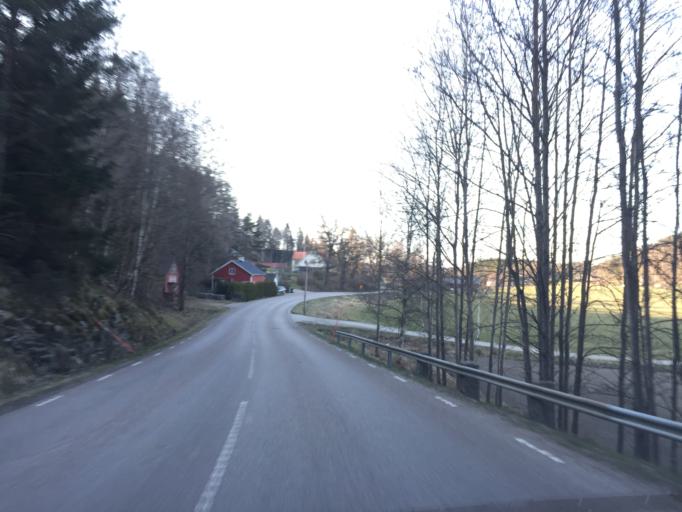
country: SE
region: Vaestra Goetaland
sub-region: Lilla Edets Kommun
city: Lilla Edet
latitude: 58.1013
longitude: 12.1171
